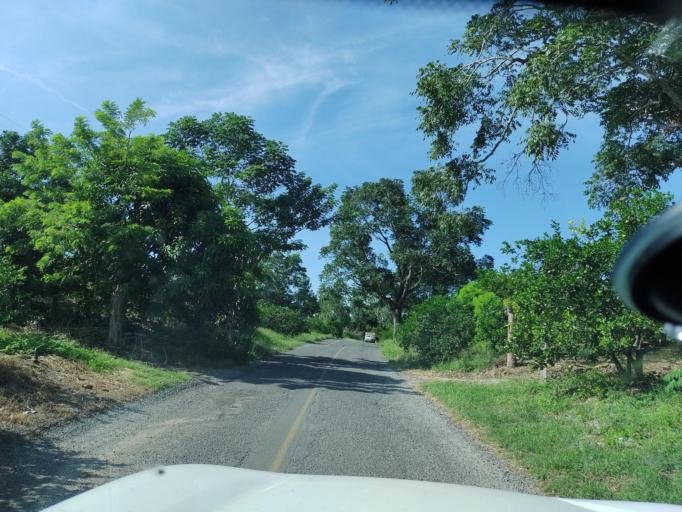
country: MX
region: Veracruz
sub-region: Martinez de la Torre
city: El Progreso
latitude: 20.1101
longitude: -96.9913
